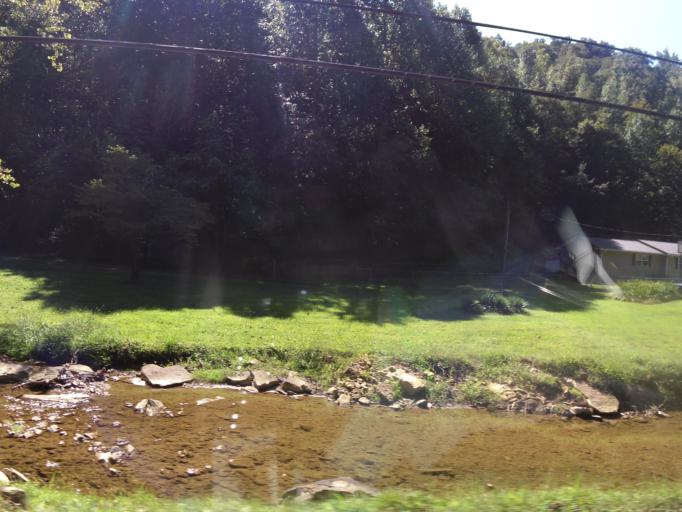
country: US
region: Kentucky
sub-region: Clay County
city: Manchester
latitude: 37.1277
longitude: -83.6263
